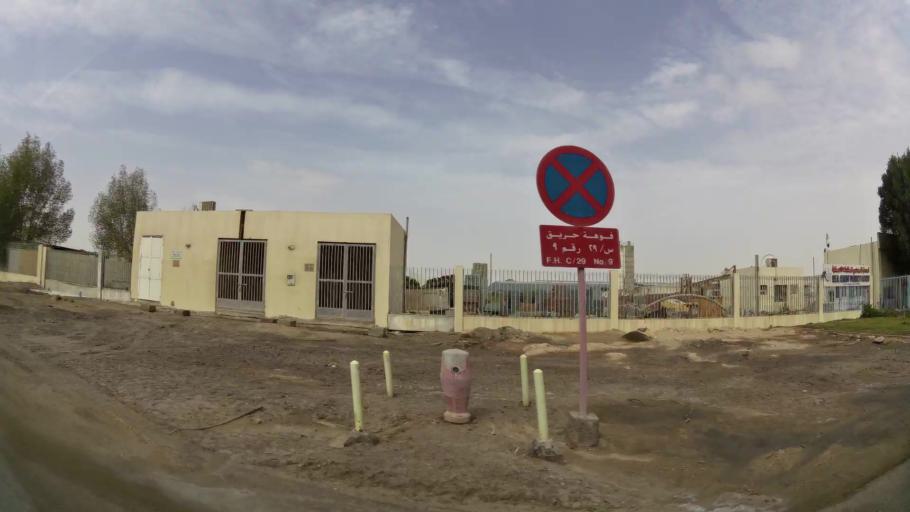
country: AE
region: Abu Dhabi
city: Abu Dhabi
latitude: 24.3292
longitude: 54.4972
